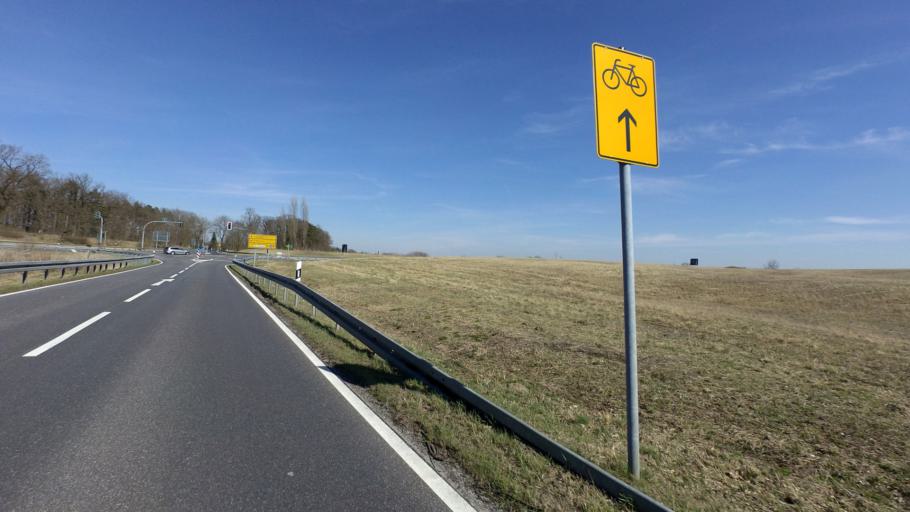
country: DE
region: Brandenburg
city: Muncheberg
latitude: 52.4988
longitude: 14.1063
